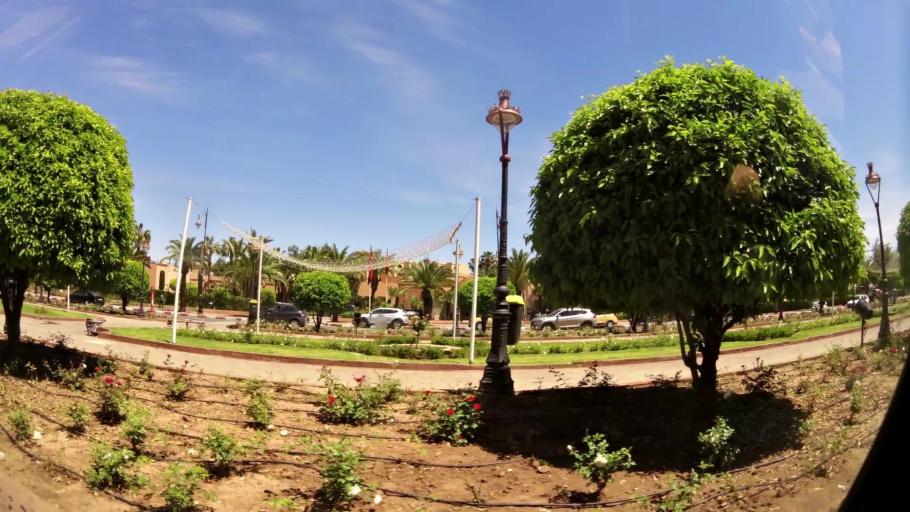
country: MA
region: Marrakech-Tensift-Al Haouz
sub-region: Marrakech
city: Marrakesh
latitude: 31.6189
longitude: -8.0089
